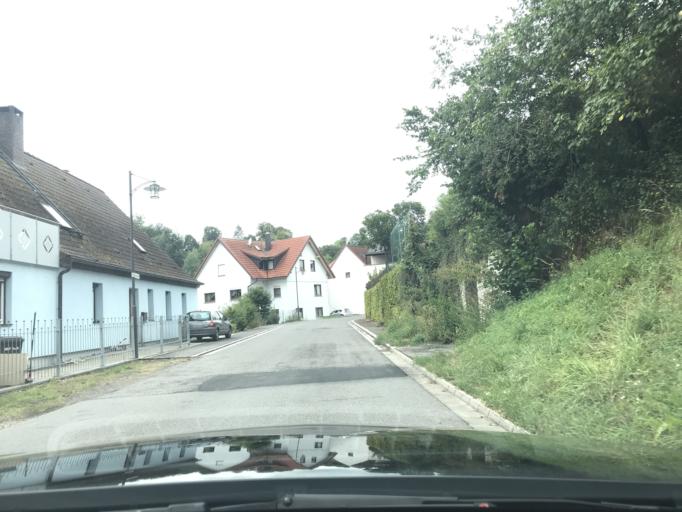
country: DE
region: Bavaria
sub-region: Regierungsbezirk Unterfranken
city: Breitbrunn
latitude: 50.0423
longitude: 10.6606
